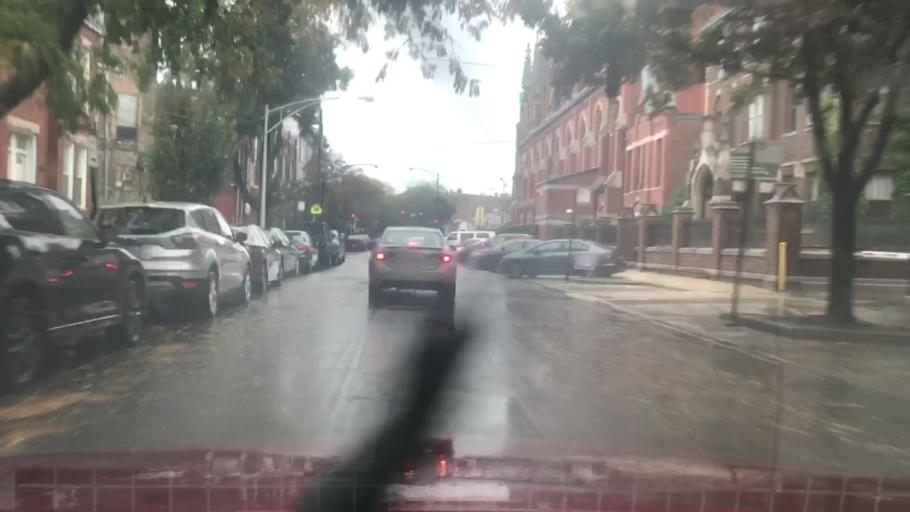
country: US
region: Illinois
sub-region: Cook County
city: Chicago
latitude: 41.9361
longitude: -87.6660
